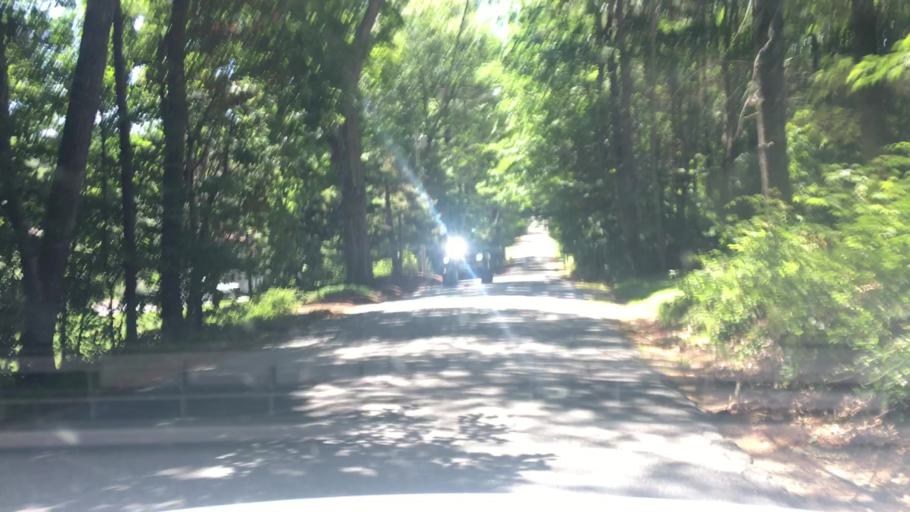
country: US
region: New Hampshire
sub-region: Merrimack County
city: Hopkinton
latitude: 43.2094
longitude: -71.6702
